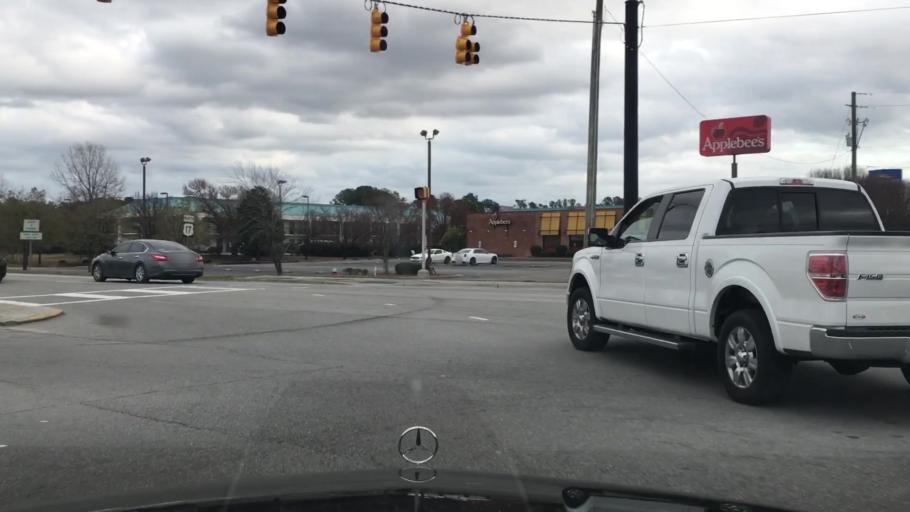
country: US
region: North Carolina
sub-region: Onslow County
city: Pumpkin Center
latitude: 34.7774
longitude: -77.3927
